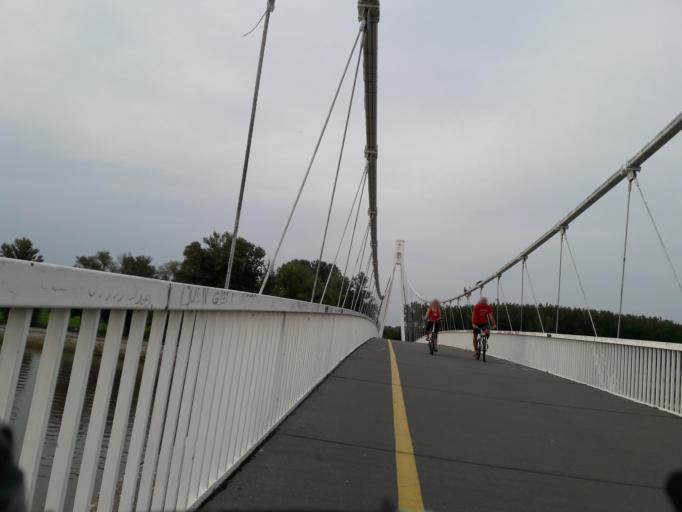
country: HR
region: Osjecko-Baranjska
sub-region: Grad Osijek
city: Osijek
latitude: 45.5632
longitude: 18.6853
